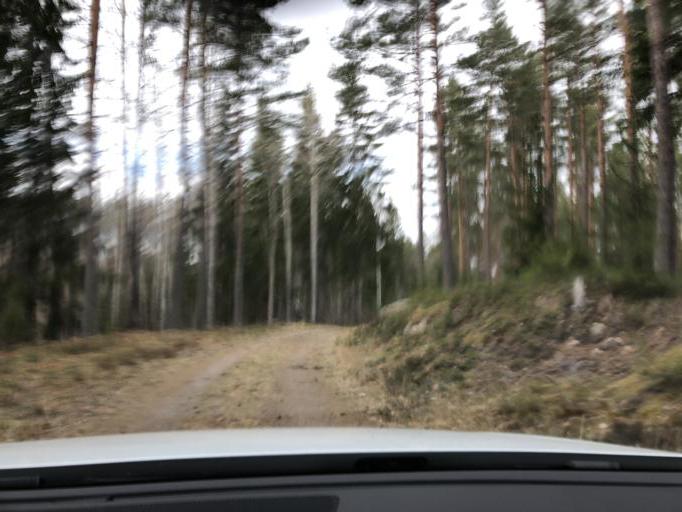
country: SE
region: Gaevleborg
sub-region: Gavle Kommun
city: Hedesunda
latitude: 60.3430
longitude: 17.0633
